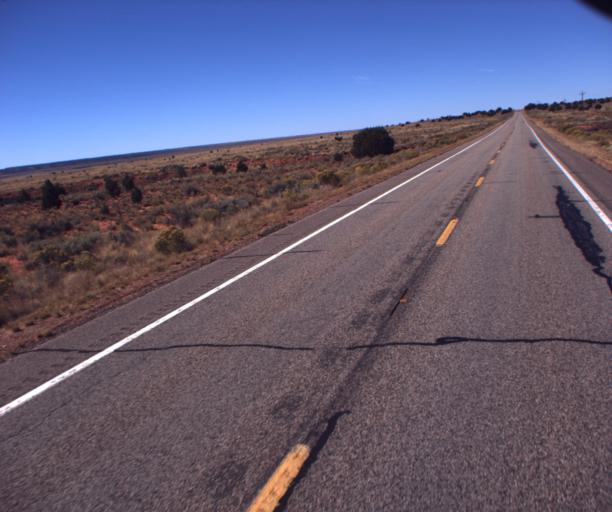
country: US
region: Arizona
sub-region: Coconino County
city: Fredonia
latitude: 36.8579
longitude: -112.7578
